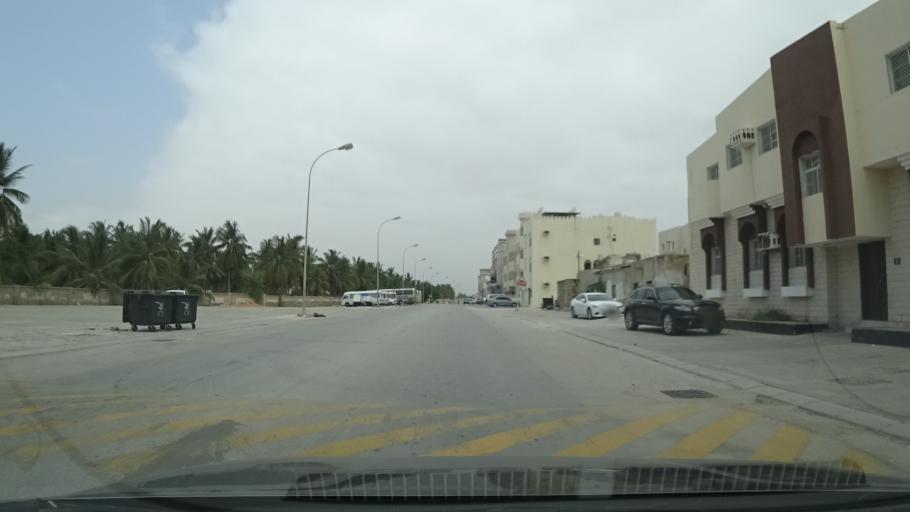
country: OM
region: Zufar
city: Salalah
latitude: 17.0227
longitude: 54.1627
